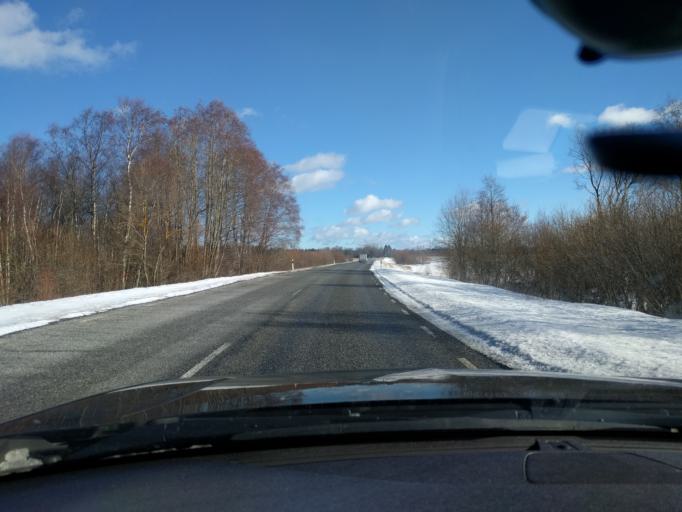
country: EE
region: Harju
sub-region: Raasiku vald
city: Raasiku
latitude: 59.4116
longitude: 25.2261
